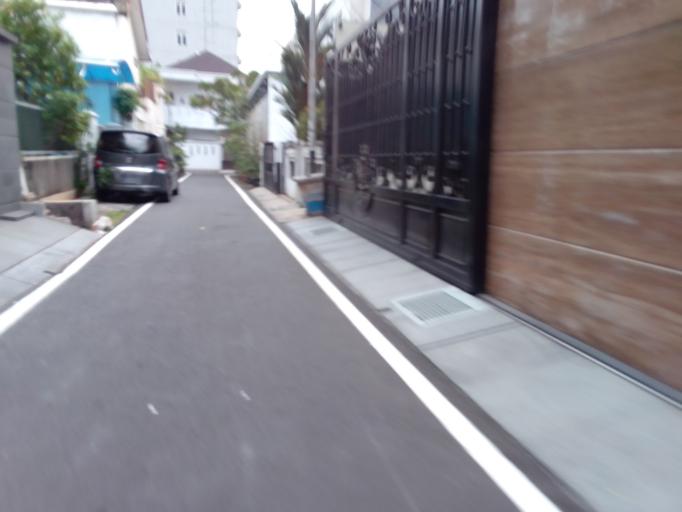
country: ID
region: Jakarta Raya
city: Jakarta
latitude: -6.1733
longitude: 106.8127
